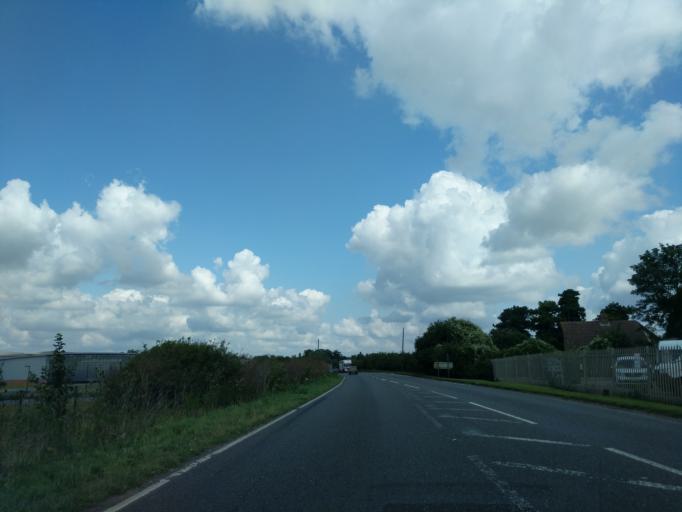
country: GB
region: England
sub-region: Suffolk
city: Exning
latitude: 52.2862
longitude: 0.3933
